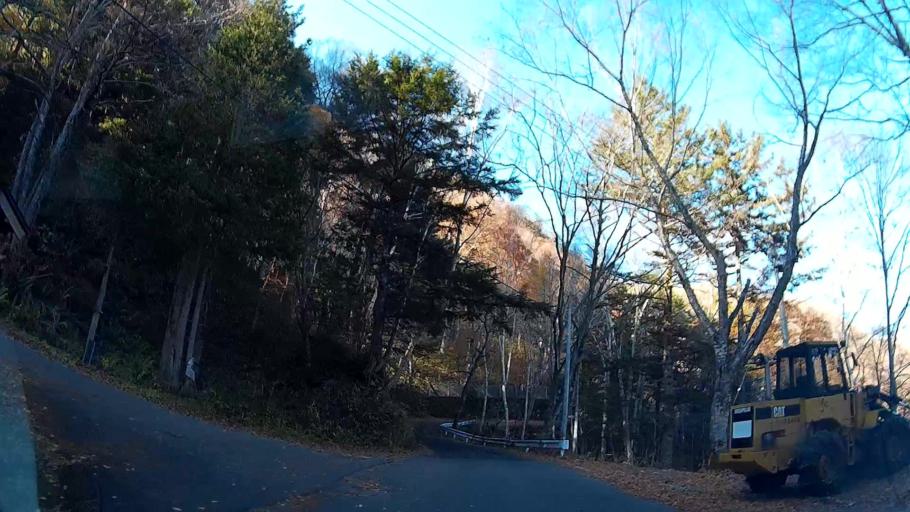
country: JP
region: Nagano
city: Hotaka
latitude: 36.2058
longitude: 137.6010
